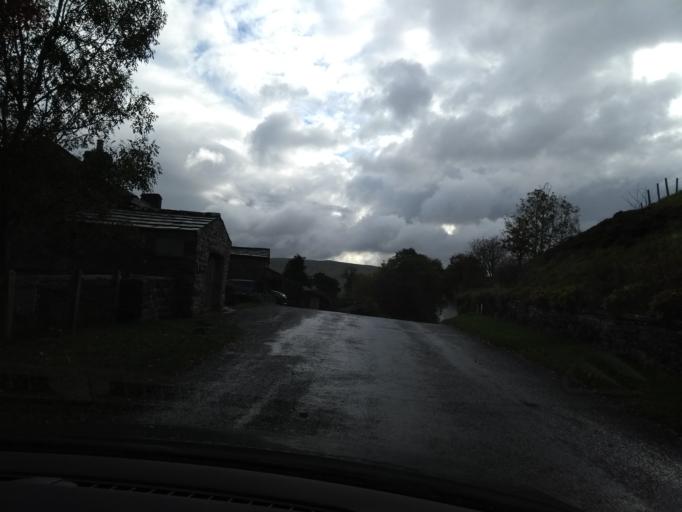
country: GB
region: England
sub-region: Cumbria
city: Kirkby Stephen
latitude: 54.3957
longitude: -2.1735
